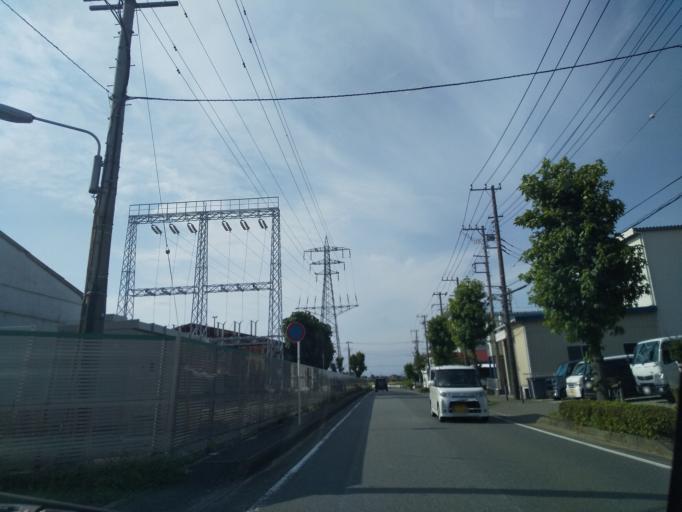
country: JP
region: Kanagawa
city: Zama
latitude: 35.4691
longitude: 139.3850
